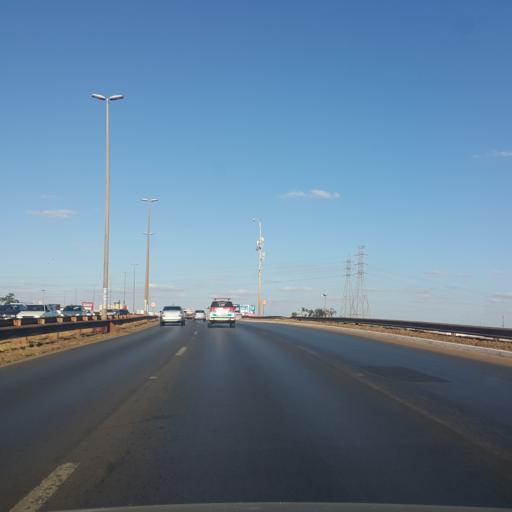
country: BR
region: Federal District
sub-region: Brasilia
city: Brasilia
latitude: -15.7950
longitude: -47.9717
